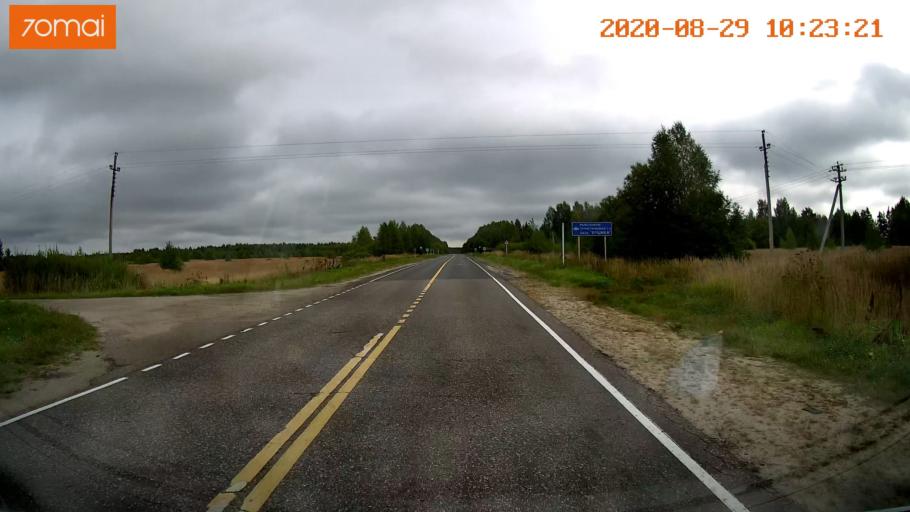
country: RU
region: Ivanovo
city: Yur'yevets
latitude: 57.3237
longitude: 42.9711
